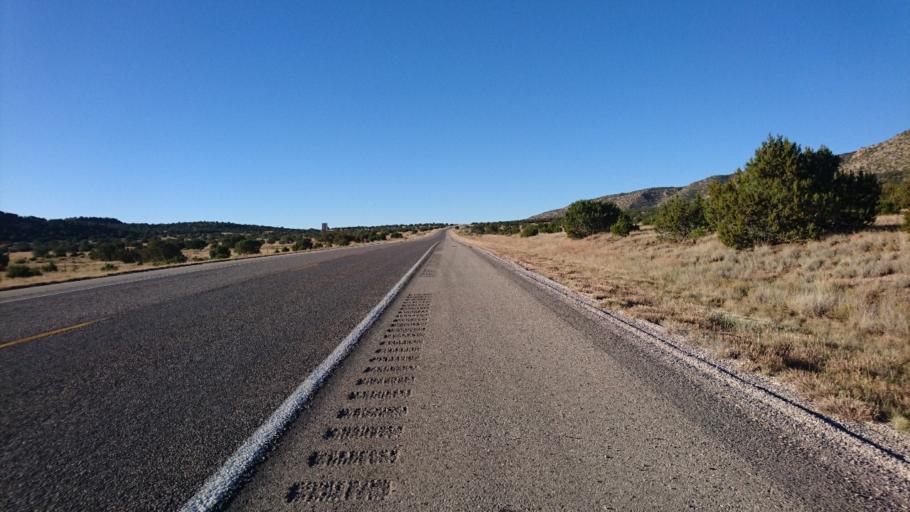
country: US
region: New Mexico
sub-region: Cibola County
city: Grants
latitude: 35.0116
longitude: -107.8895
